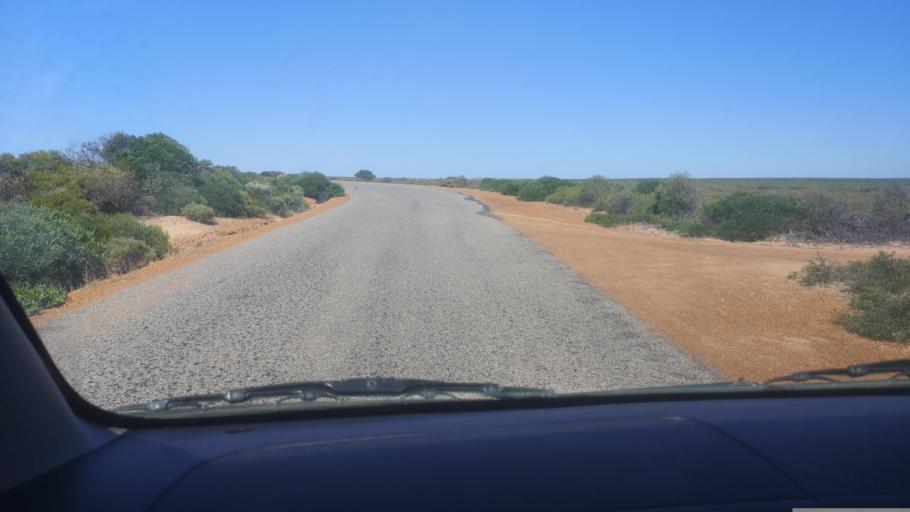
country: AU
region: Western Australia
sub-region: Northampton Shire
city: Kalbarri
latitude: -27.8275
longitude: 114.1154
